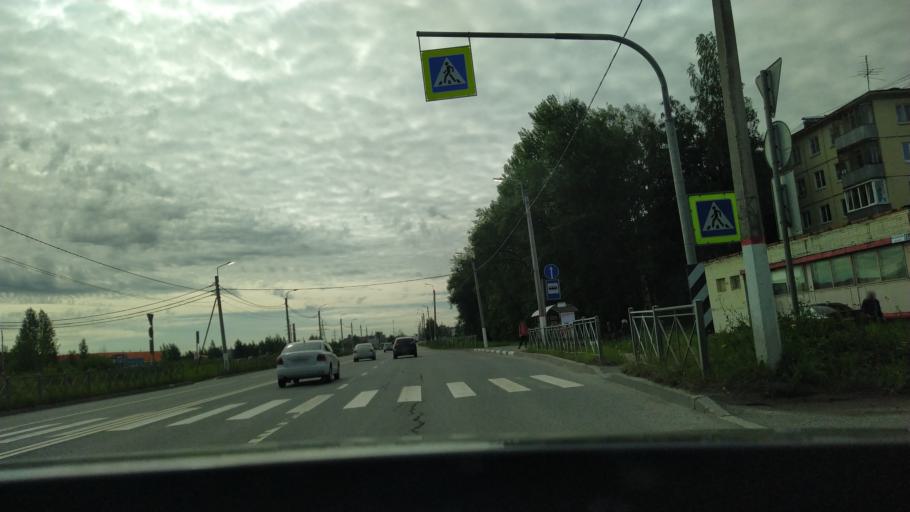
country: RU
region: Leningrad
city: Tosno
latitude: 59.5566
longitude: 30.8482
